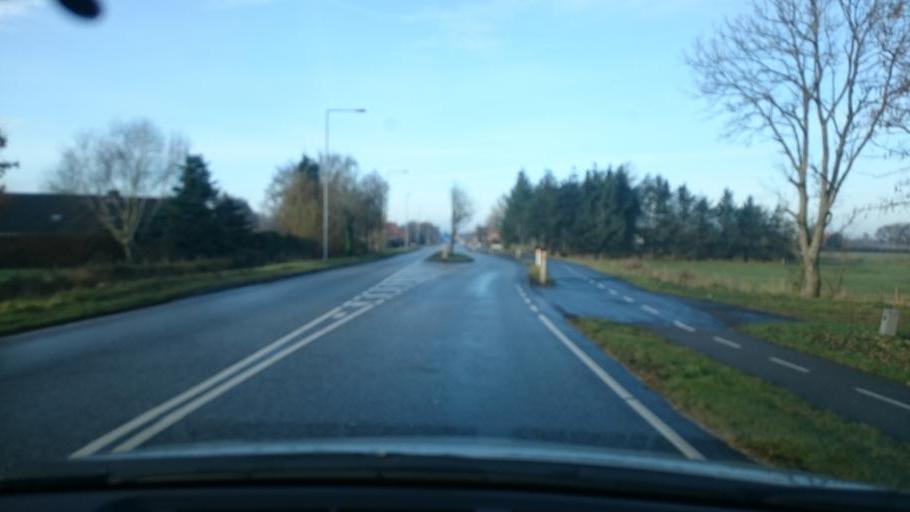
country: DK
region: South Denmark
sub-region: Esbjerg Kommune
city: Ribe
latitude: 55.3169
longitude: 8.7773
